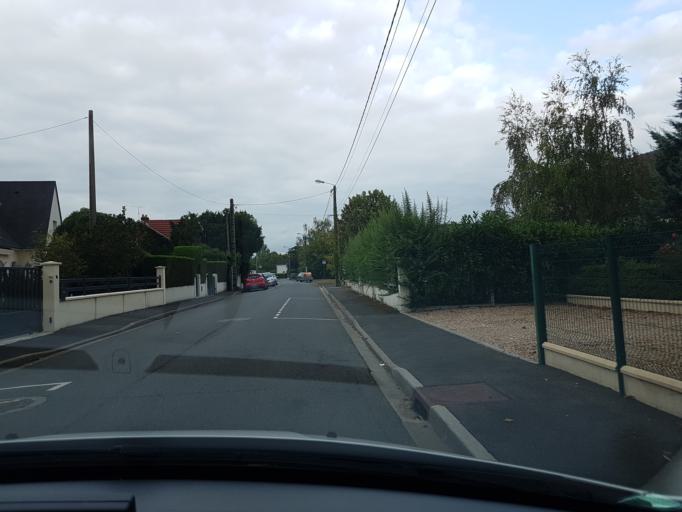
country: FR
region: Centre
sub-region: Departement d'Indre-et-Loire
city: Saint-Avertin
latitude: 47.3644
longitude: 0.7470
